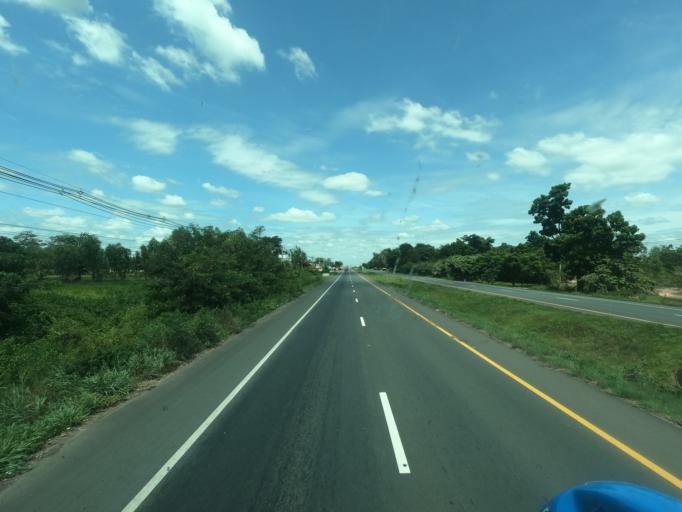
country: TH
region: Surin
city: Prasat
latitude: 14.6177
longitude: 103.3597
